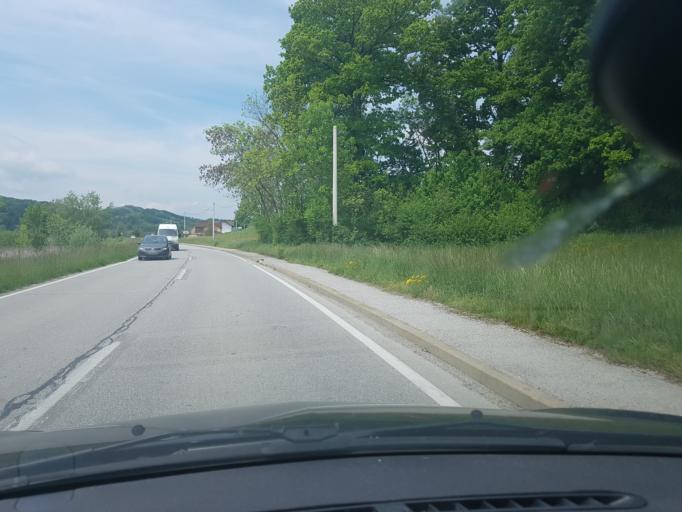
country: HR
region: Krapinsko-Zagorska
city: Pregrada
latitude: 46.1451
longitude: 15.7795
